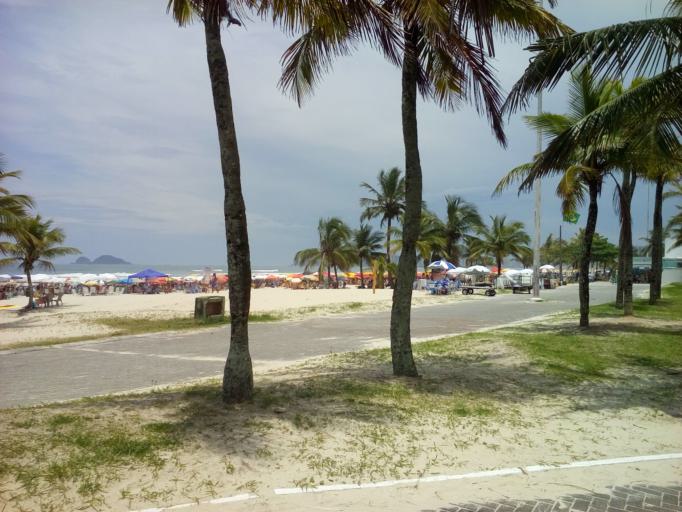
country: BR
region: Sao Paulo
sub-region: Guaruja
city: Guaruja
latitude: -23.9868
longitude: -46.2300
